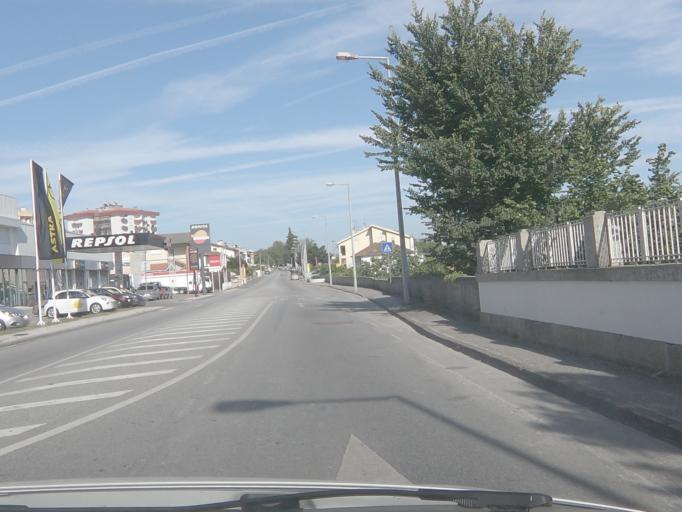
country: PT
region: Viseu
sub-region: Viseu
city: Viseu
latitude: 40.6548
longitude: -7.8969
